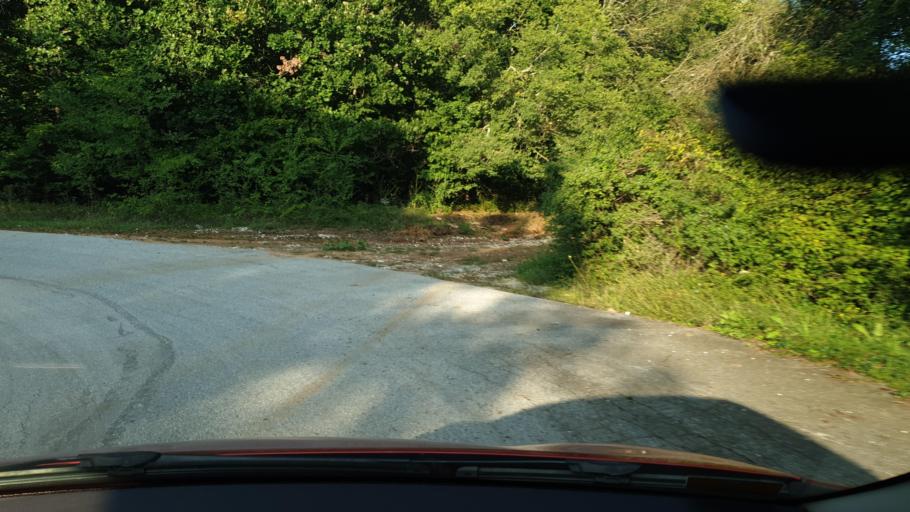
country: GR
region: Central Macedonia
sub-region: Nomos Chalkidikis
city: Galatista
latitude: 40.5329
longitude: 23.2781
